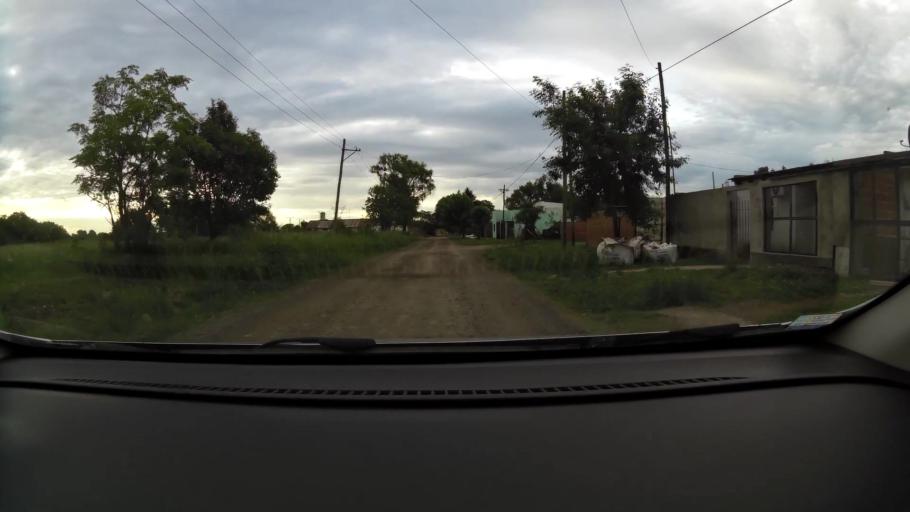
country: AR
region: Buenos Aires
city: San Nicolas de los Arroyos
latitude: -33.3676
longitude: -60.2035
